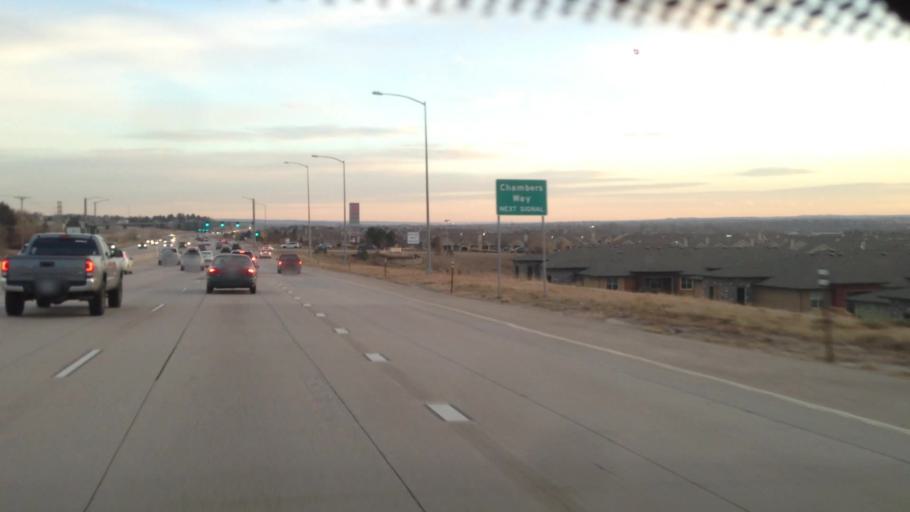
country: US
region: Colorado
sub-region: Arapahoe County
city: Dove Valley
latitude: 39.5901
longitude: -104.7996
